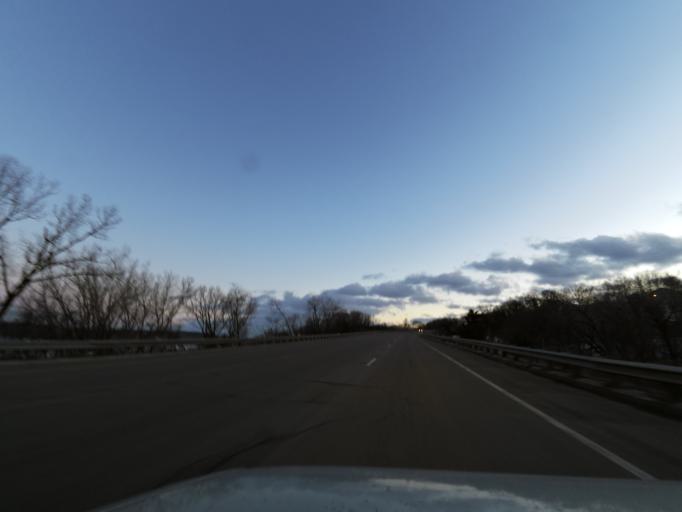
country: US
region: Wisconsin
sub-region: Saint Croix County
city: North Hudson
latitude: 44.9944
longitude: -92.7777
